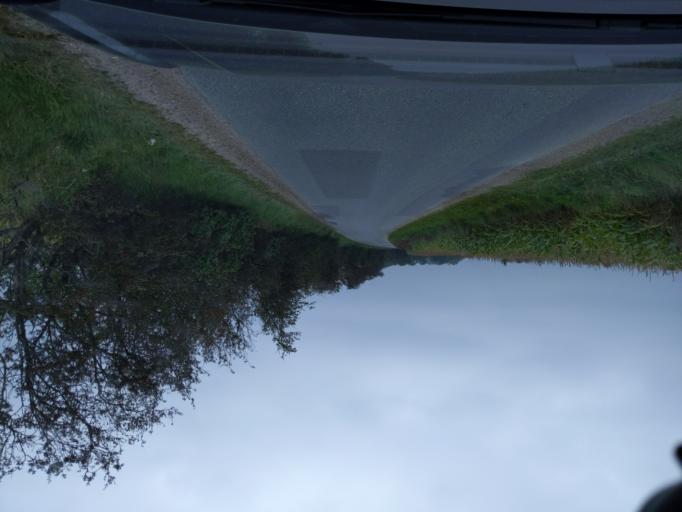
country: DK
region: Central Jutland
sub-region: Viborg Kommune
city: Stoholm
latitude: 56.5100
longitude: 9.2538
